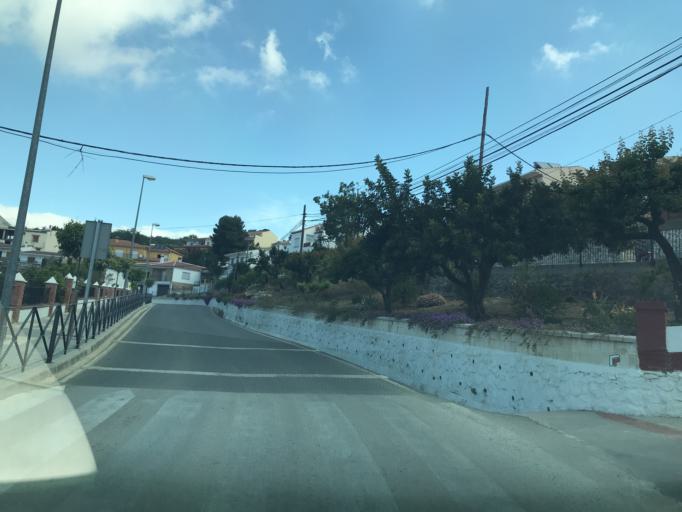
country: ES
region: Andalusia
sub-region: Provincia de Malaga
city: Periana
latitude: 36.9292
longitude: -4.1893
